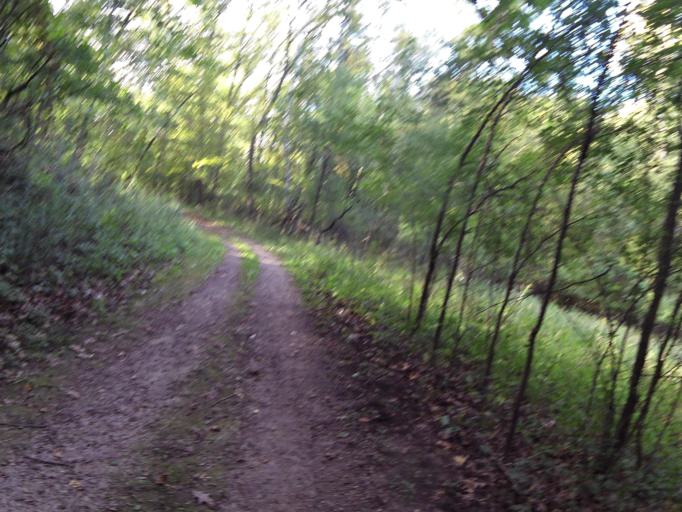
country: US
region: Minnesota
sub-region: Washington County
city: Afton
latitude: 44.8604
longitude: -92.7963
